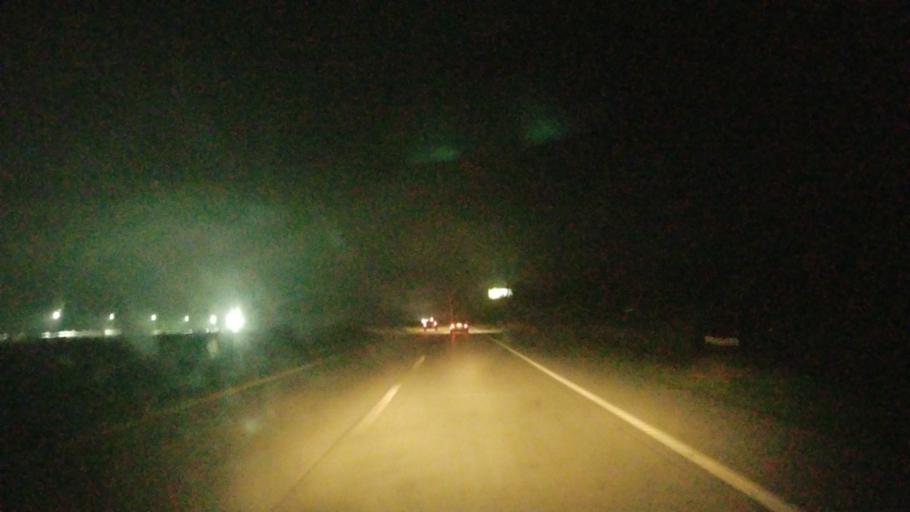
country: US
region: Missouri
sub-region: Lincoln County
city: Troy
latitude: 39.0858
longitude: -90.9708
